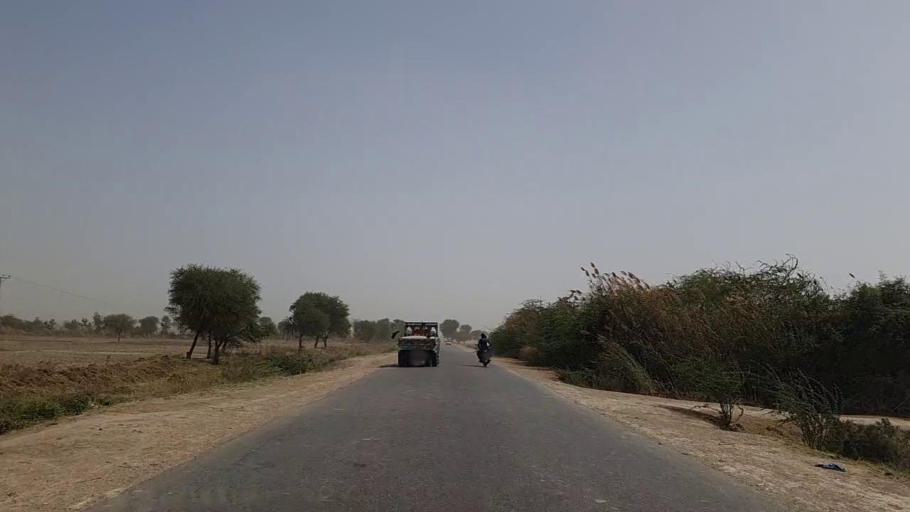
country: PK
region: Sindh
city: Talhar
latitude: 24.8741
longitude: 68.8376
